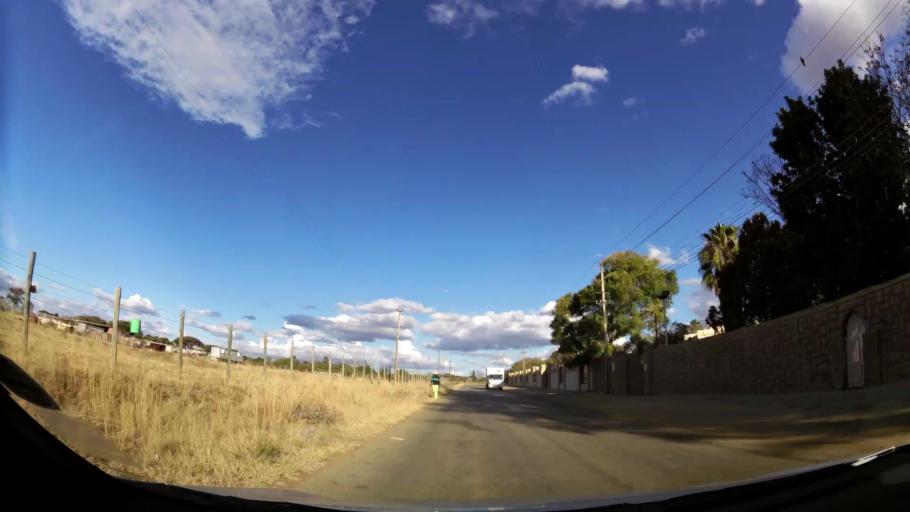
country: ZA
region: Limpopo
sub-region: Capricorn District Municipality
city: Polokwane
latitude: -23.9317
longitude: 29.4294
